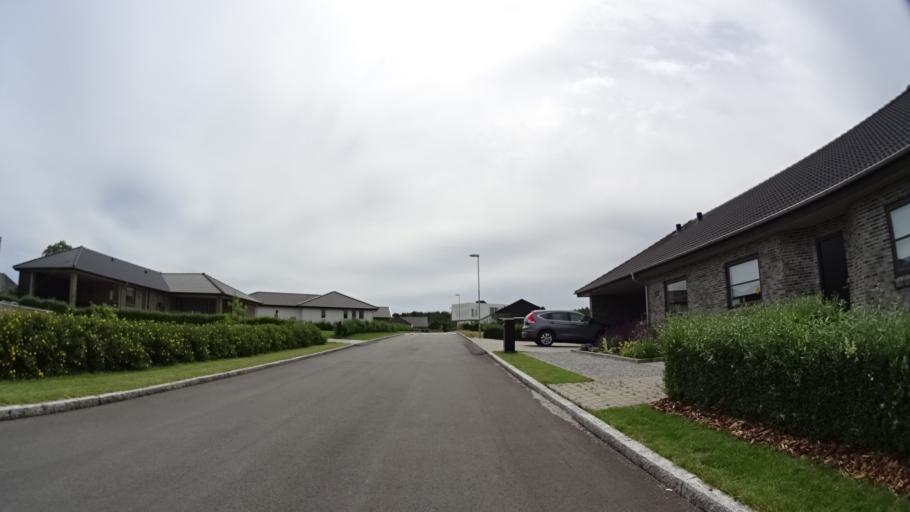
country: DK
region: Central Jutland
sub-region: Arhus Kommune
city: Stavtrup
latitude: 56.1213
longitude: 10.1209
